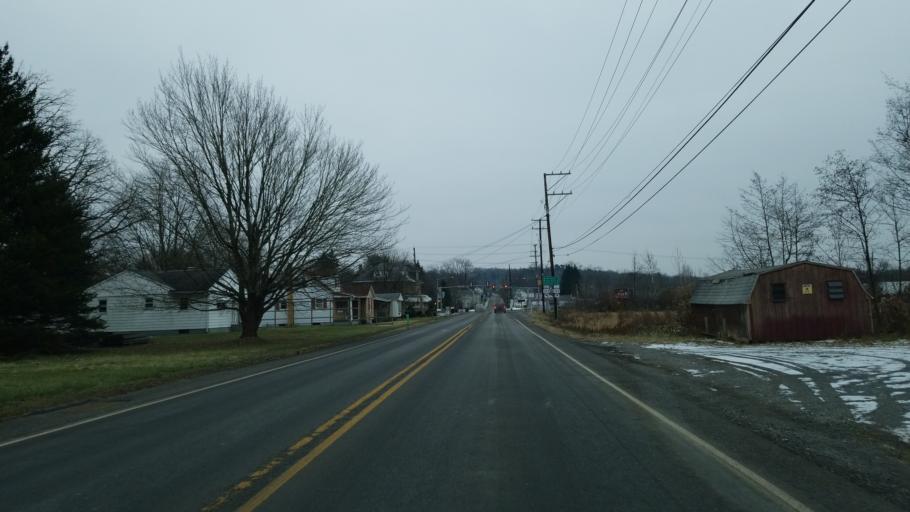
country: US
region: Pennsylvania
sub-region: Centre County
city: Philipsburg
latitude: 40.9063
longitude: -78.2217
